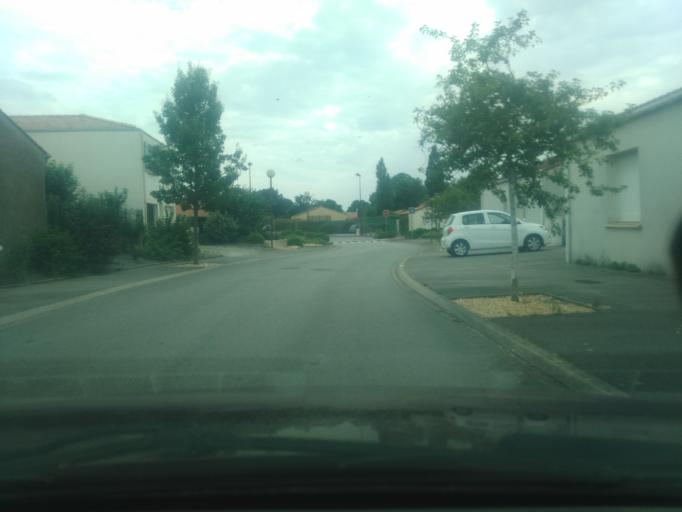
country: FR
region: Pays de la Loire
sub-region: Departement de la Vendee
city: La Ferriere
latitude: 46.7133
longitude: -1.3067
